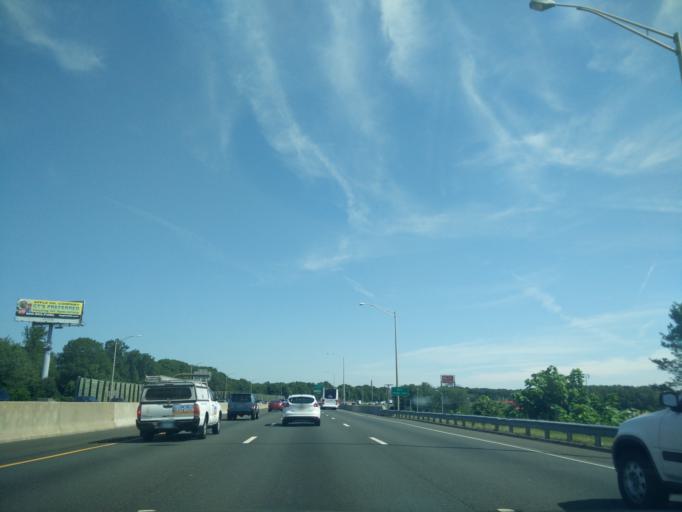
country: US
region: Connecticut
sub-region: New Haven County
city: West Haven
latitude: 41.2725
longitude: -72.9706
